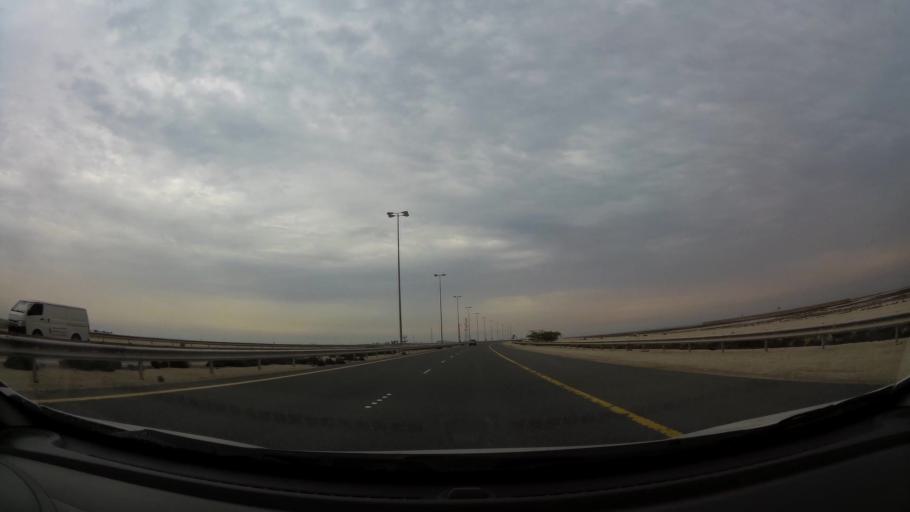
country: BH
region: Central Governorate
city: Dar Kulayb
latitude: 25.8557
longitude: 50.5848
